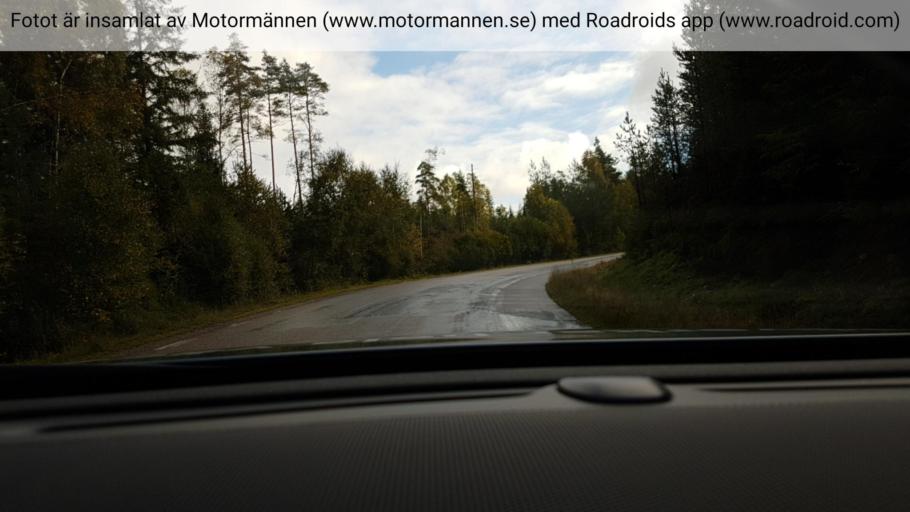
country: SE
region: Vaestra Goetaland
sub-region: Marks Kommun
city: Fritsla
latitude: 57.4023
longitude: 12.8661
